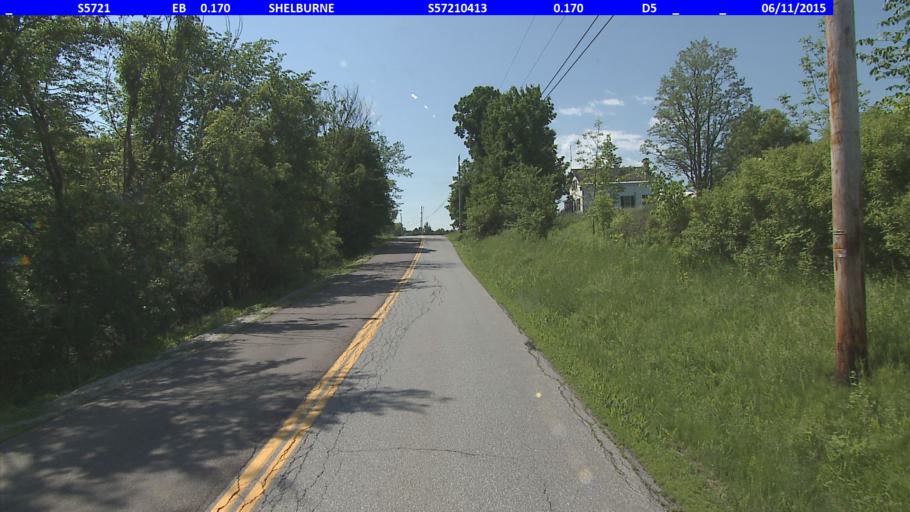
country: US
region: Vermont
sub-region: Chittenden County
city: Burlington
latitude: 44.3683
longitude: -73.2145
